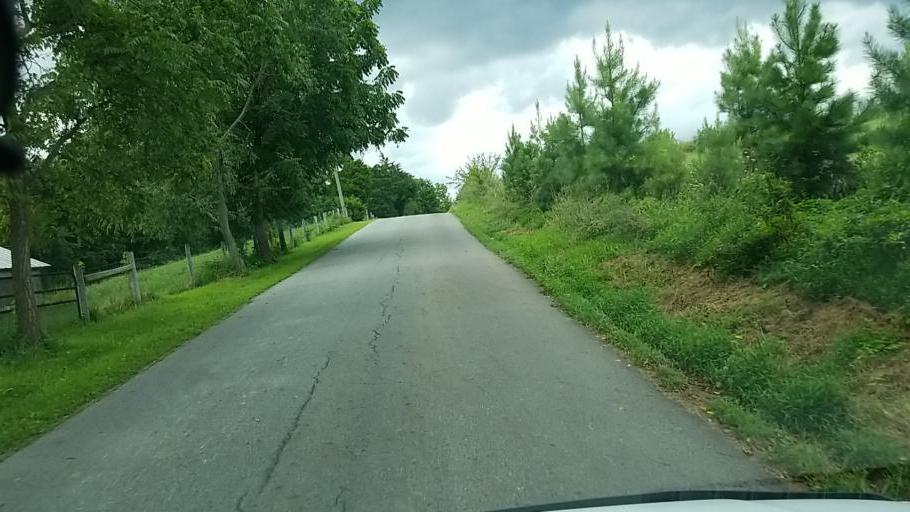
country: US
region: Pennsylvania
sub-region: Dauphin County
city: Elizabethville
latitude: 40.5913
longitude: -76.8022
